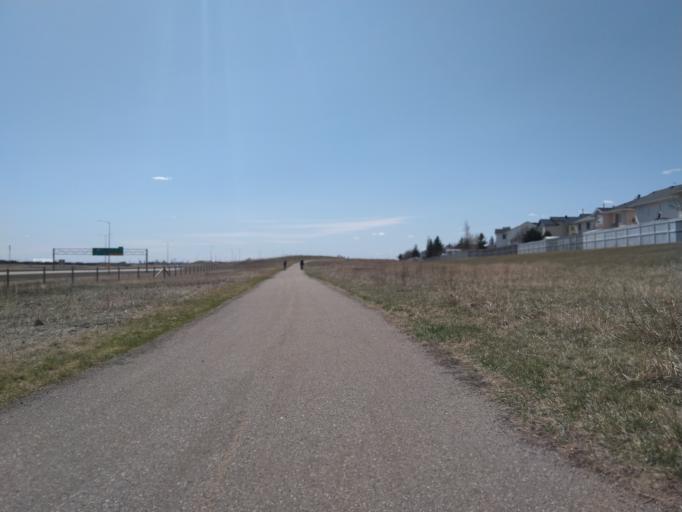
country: CA
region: Alberta
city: Chestermere
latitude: 51.0771
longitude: -113.9227
